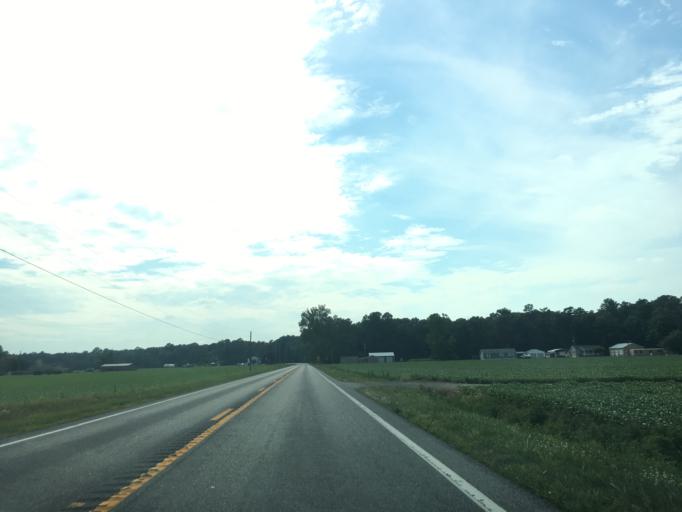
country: US
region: Delaware
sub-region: Sussex County
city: Georgetown
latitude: 38.7456
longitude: -75.4507
